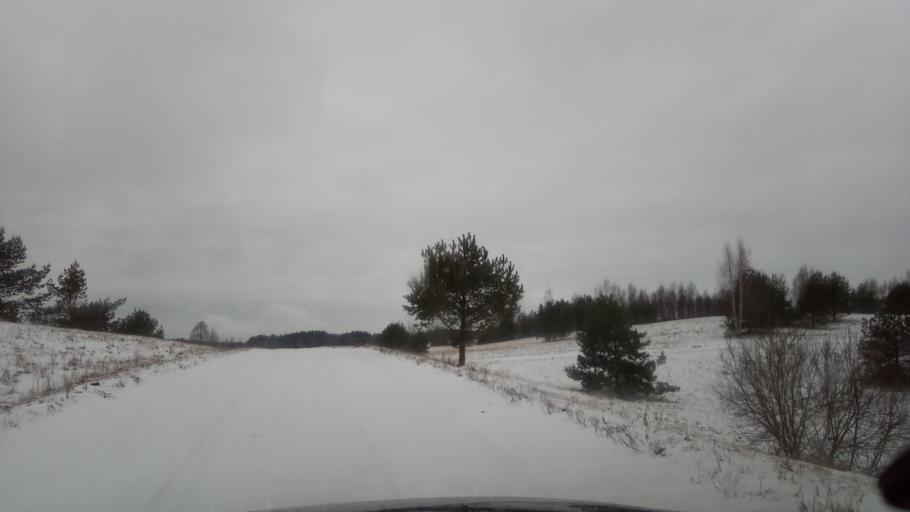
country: LT
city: Zarasai
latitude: 55.6844
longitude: 26.1049
